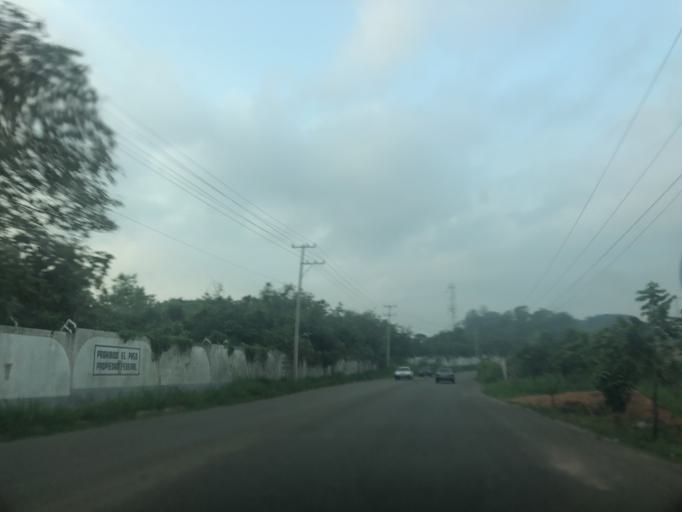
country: MX
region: Chiapas
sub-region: Reforma
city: El Carmen (El Limon)
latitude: 17.8637
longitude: -93.1567
